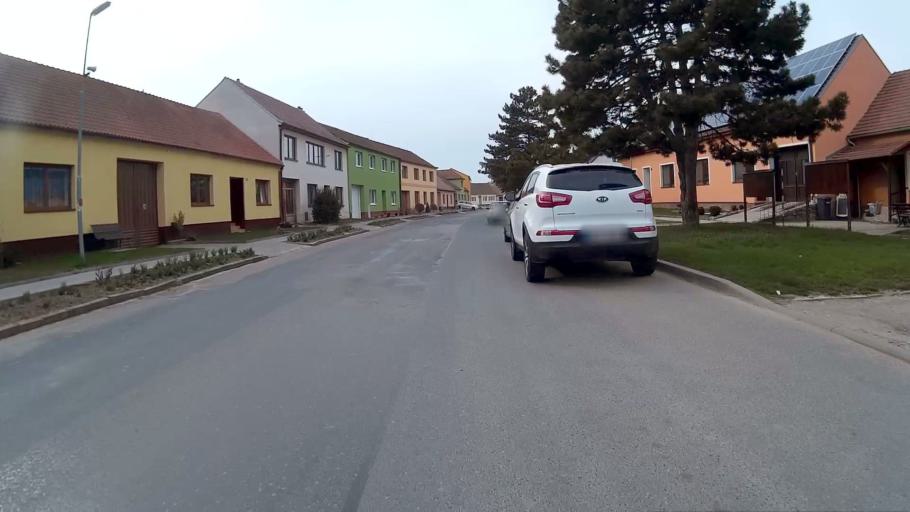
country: CZ
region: South Moravian
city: Dolni Kounice
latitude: 49.0710
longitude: 16.4422
